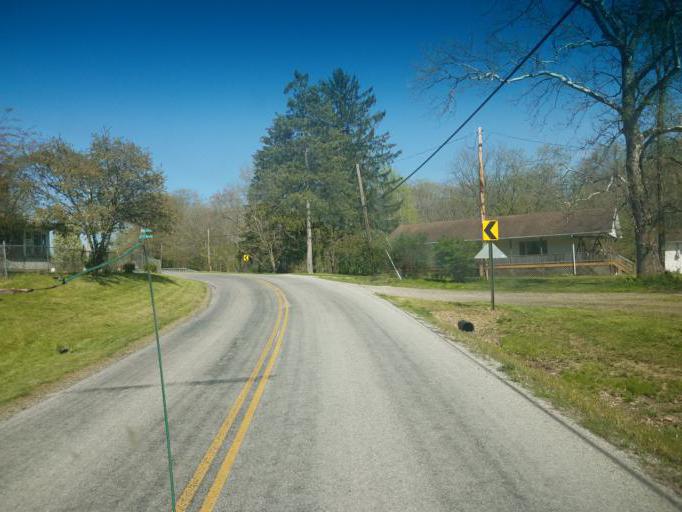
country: US
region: Ohio
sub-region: Medina County
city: Lodi
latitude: 40.9870
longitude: -82.0062
